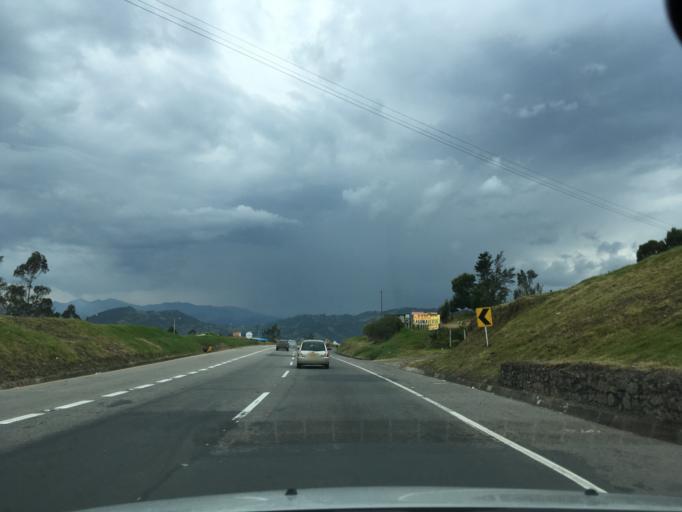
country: CO
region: Boyaca
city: Ventaquemada
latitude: 5.3862
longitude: -73.5017
